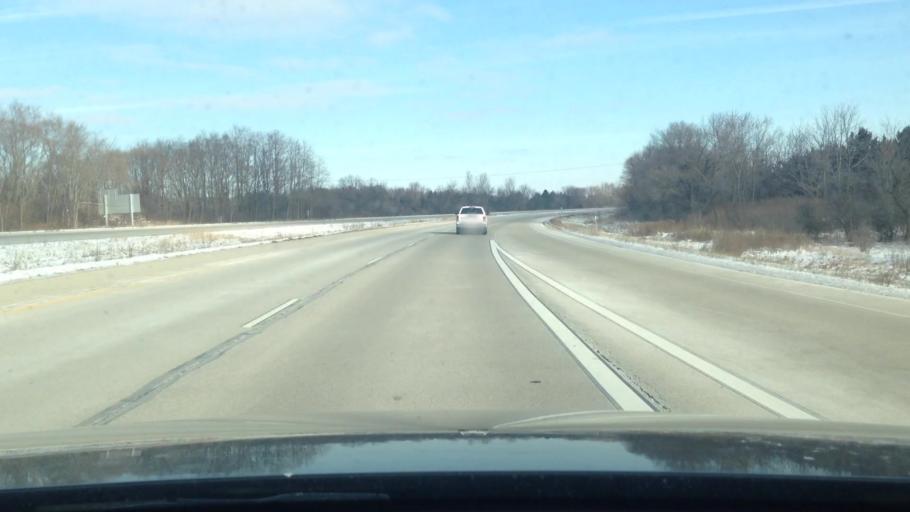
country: US
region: Wisconsin
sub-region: Walworth County
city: East Troy
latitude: 42.7968
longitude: -88.3828
